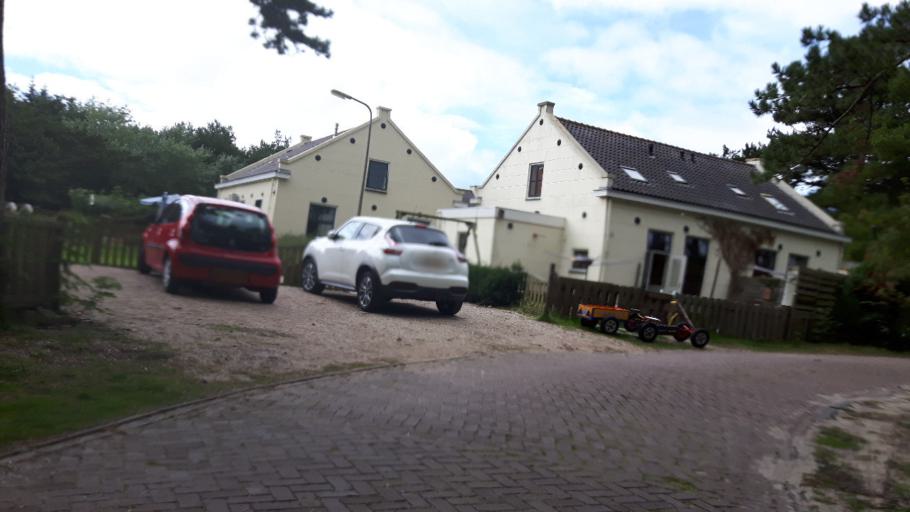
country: NL
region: Friesland
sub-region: Gemeente Ameland
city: Hollum
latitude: 53.4484
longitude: 5.6274
